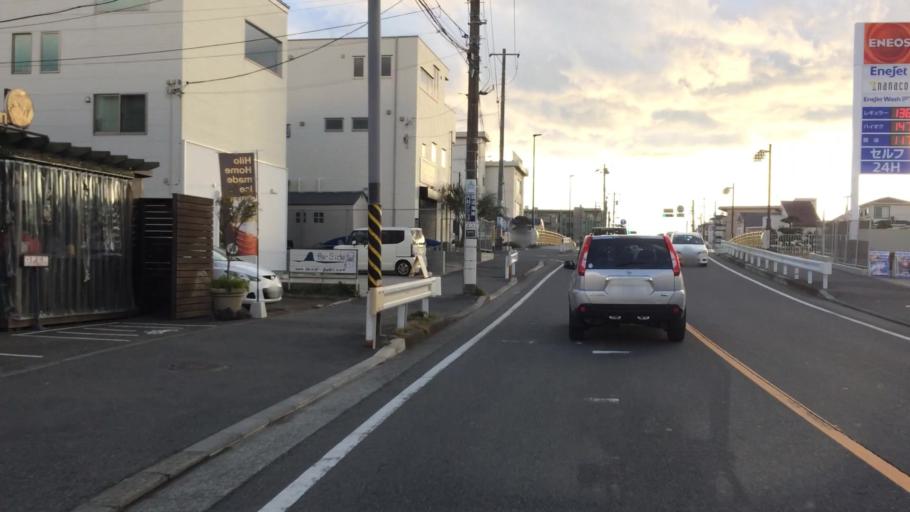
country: JP
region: Kanagawa
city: Fujisawa
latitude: 35.3199
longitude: 139.4640
